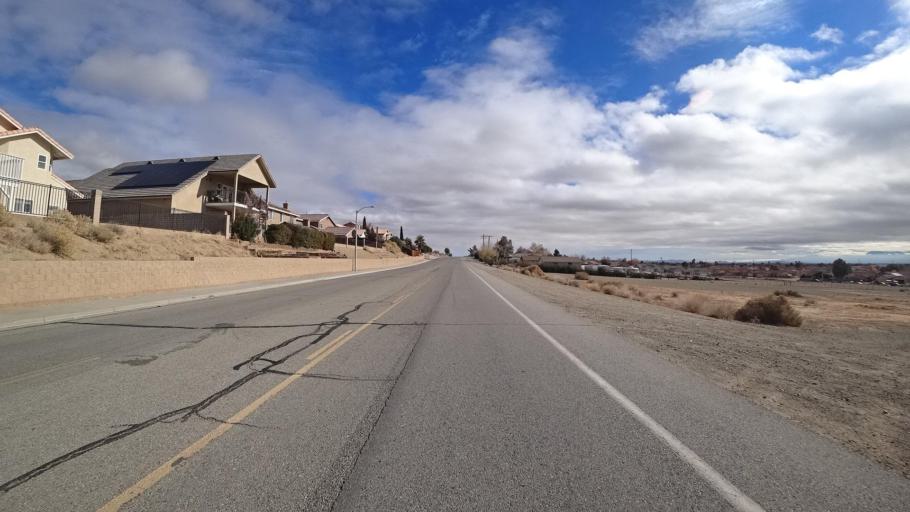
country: US
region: California
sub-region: Kern County
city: Rosamond
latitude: 34.8714
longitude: -118.1825
